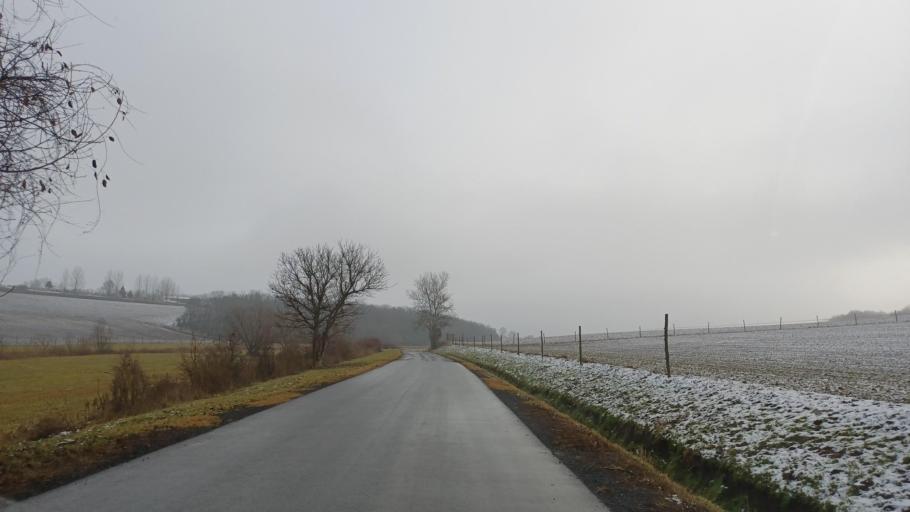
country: HU
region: Tolna
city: Gyonk
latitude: 46.5949
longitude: 18.4995
